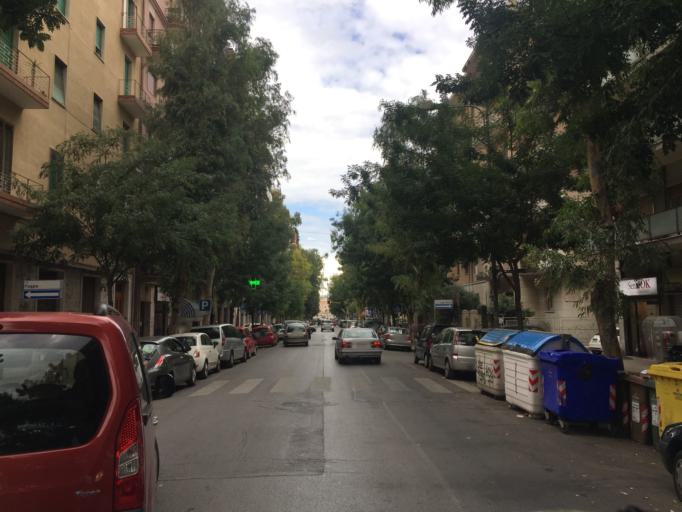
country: IT
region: Apulia
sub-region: Provincia di Bari
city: Bari
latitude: 41.1133
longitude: 16.8635
